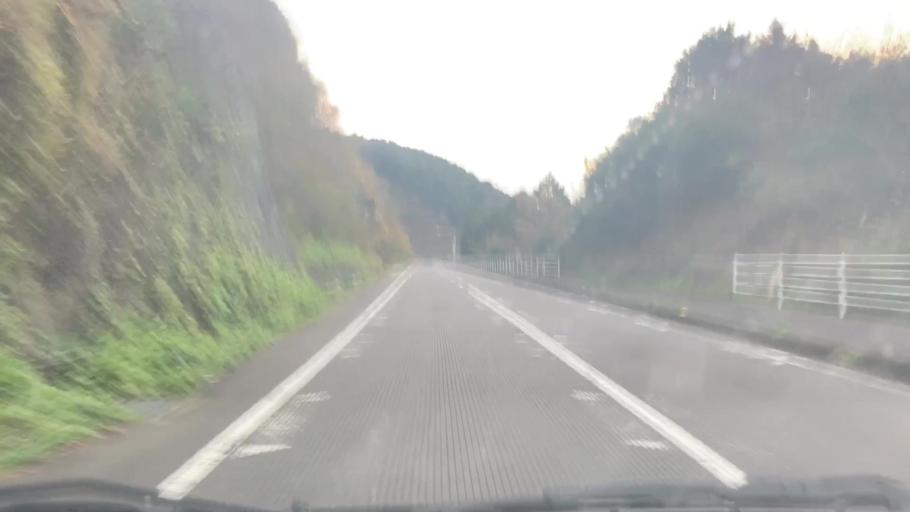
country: JP
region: Saga Prefecture
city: Kashima
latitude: 33.0444
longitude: 130.0717
